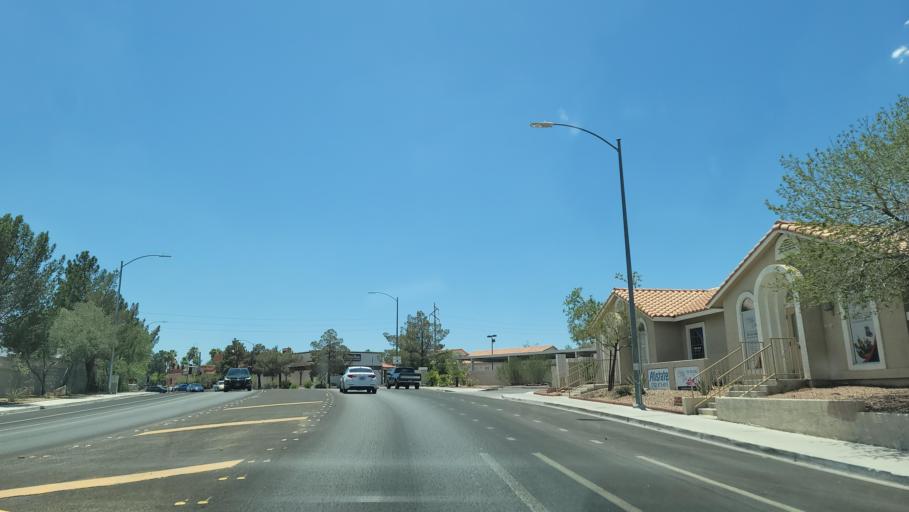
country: US
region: Nevada
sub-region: Clark County
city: Spring Valley
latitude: 36.1608
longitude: -115.2706
